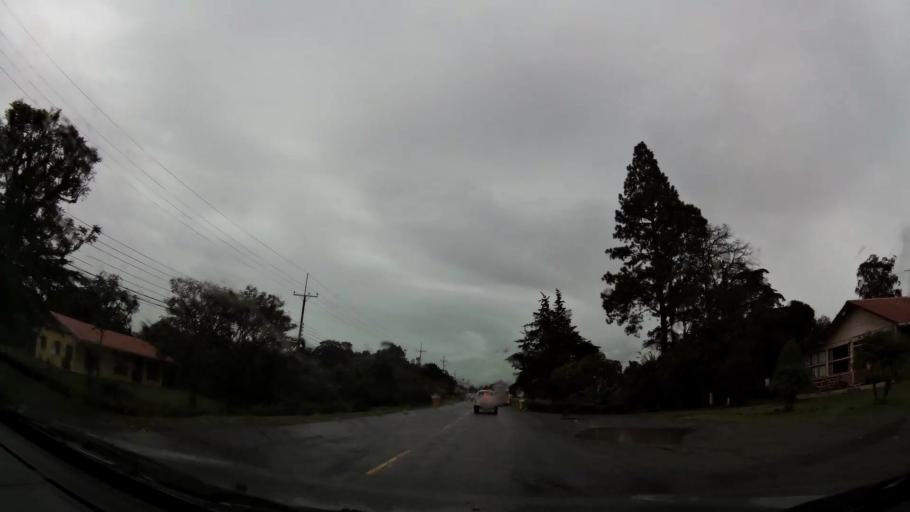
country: PA
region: Chiriqui
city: Volcan
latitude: 8.7737
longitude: -82.6369
